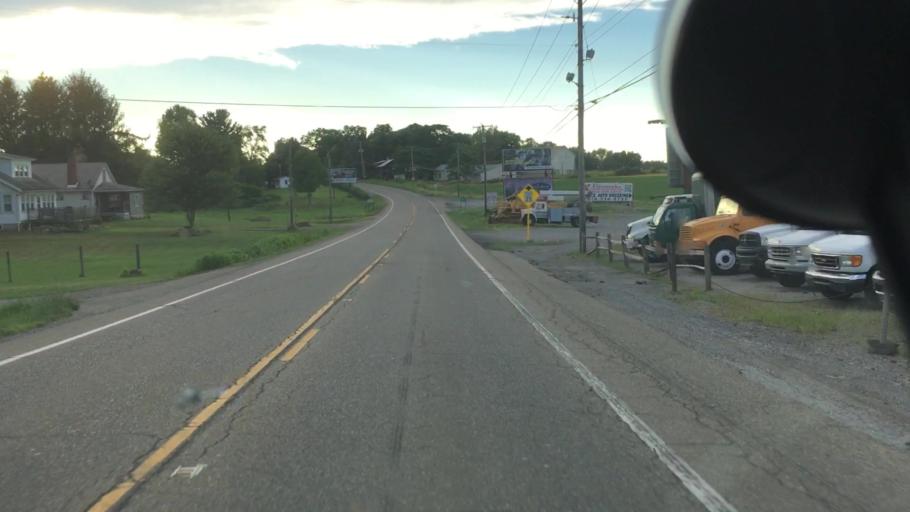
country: US
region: Ohio
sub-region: Columbiana County
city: East Palestine
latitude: 40.8627
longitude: -80.5526
